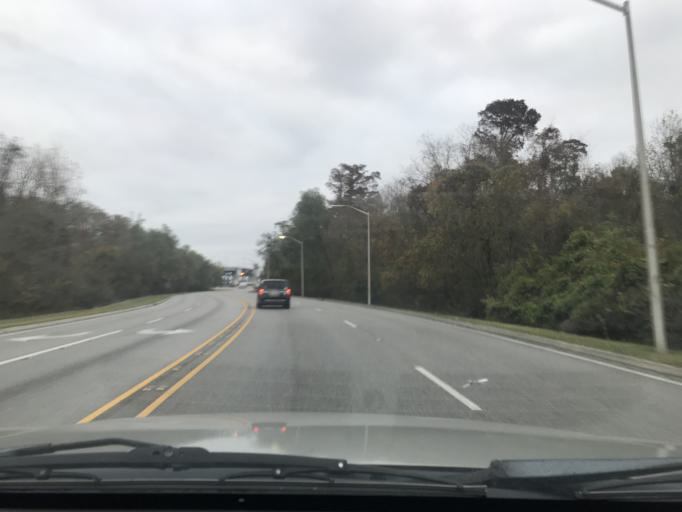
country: US
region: Louisiana
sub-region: Jefferson Parish
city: Woodmere
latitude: 29.8687
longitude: -90.0746
